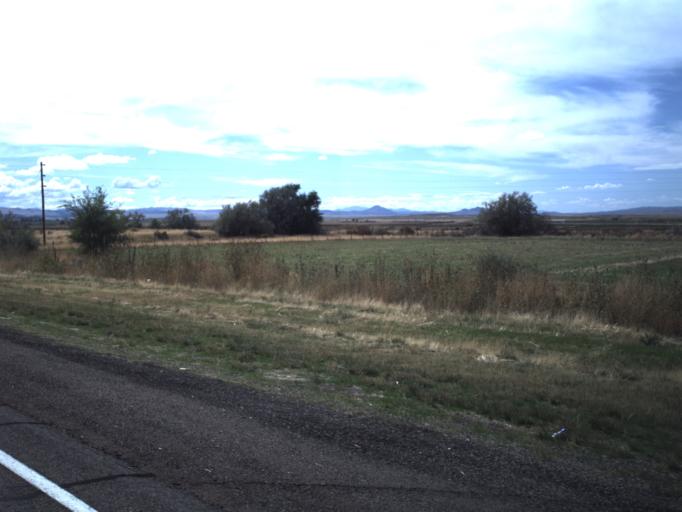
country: US
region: Utah
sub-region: Millard County
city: Fillmore
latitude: 38.8805
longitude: -112.4113
